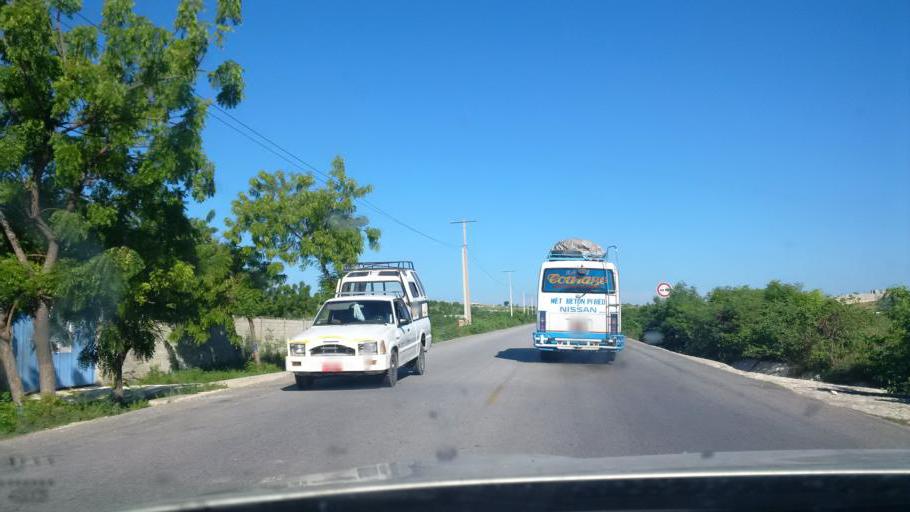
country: HT
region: Ouest
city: Cabaret
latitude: 18.7260
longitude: -72.3866
